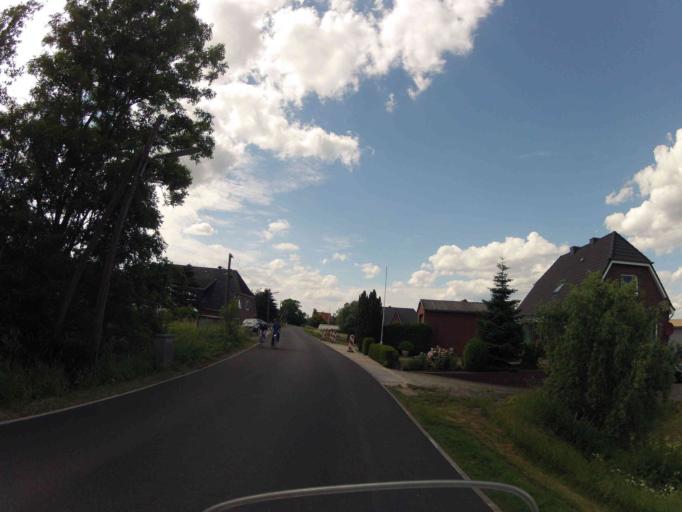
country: DE
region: Hamburg
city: Bergedorf
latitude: 53.4543
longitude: 10.1540
